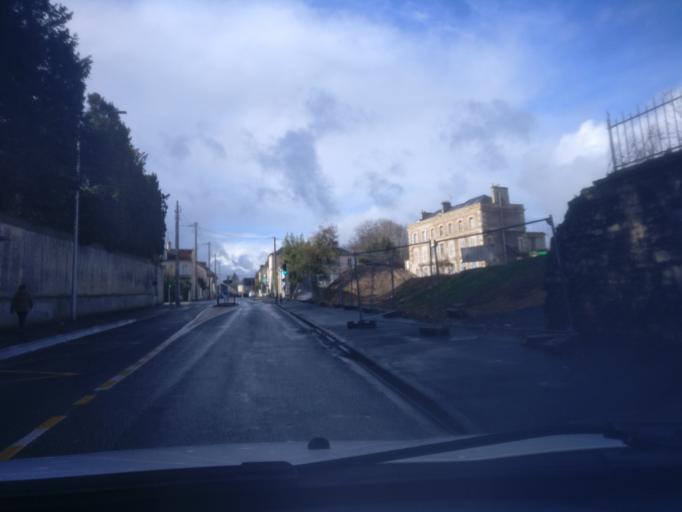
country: FR
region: Lower Normandy
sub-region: Departement du Calvados
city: Caen
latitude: 49.1905
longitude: -0.3727
